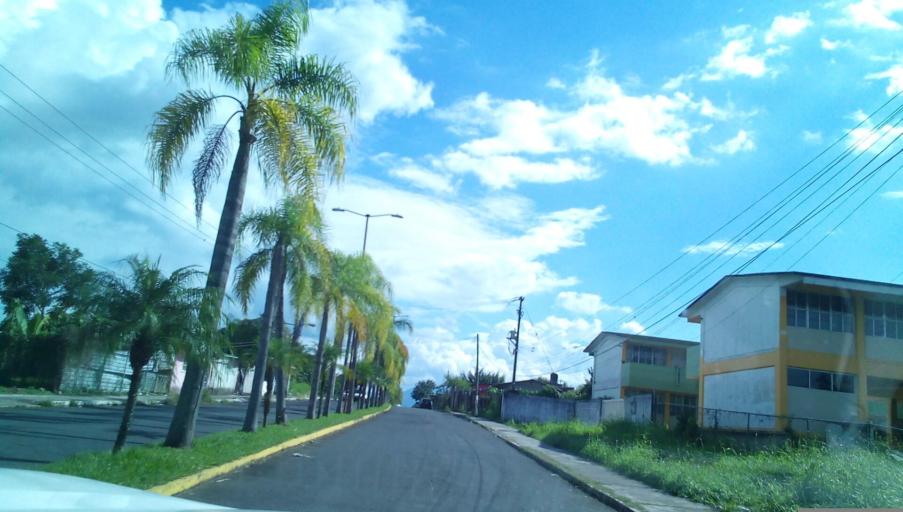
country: MX
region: Veracruz
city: Cordoba
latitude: 18.8915
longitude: -96.9210
